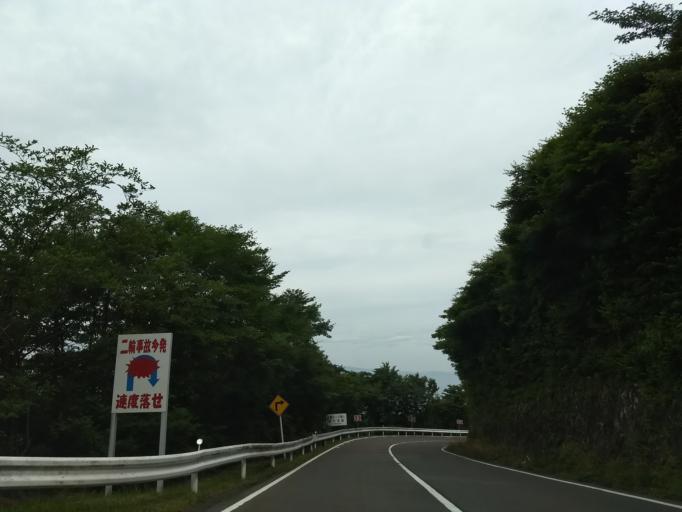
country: JP
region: Kanagawa
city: Hakone
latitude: 35.2194
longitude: 138.9810
